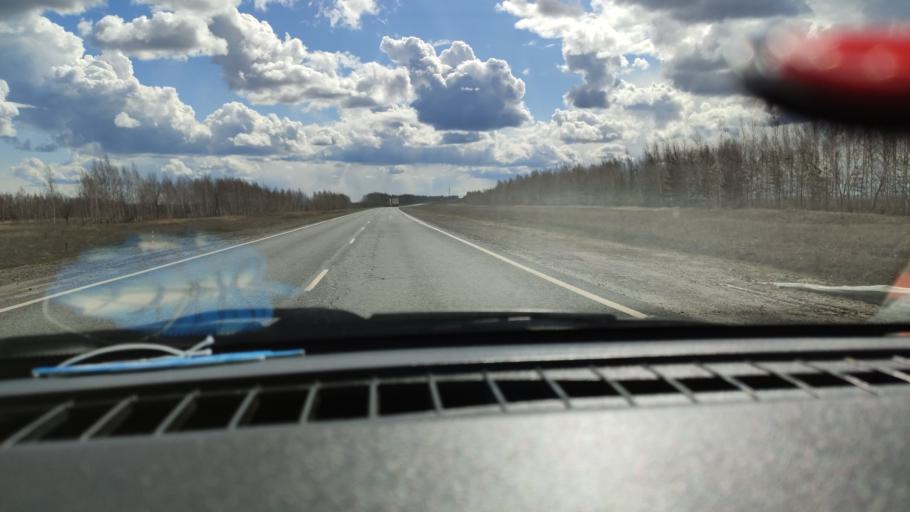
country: RU
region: Saratov
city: Dukhovnitskoye
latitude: 52.8490
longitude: 48.2554
